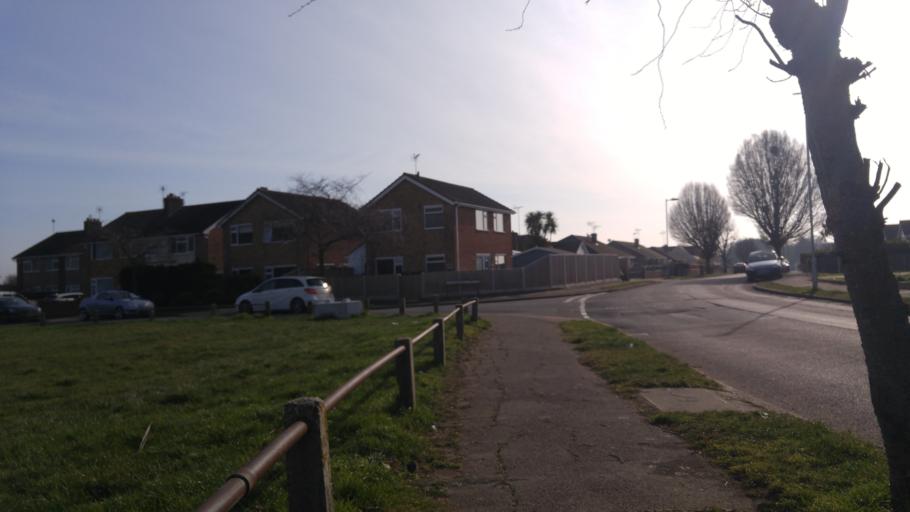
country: GB
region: England
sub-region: Essex
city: Clacton-on-Sea
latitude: 51.8139
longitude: 1.1657
